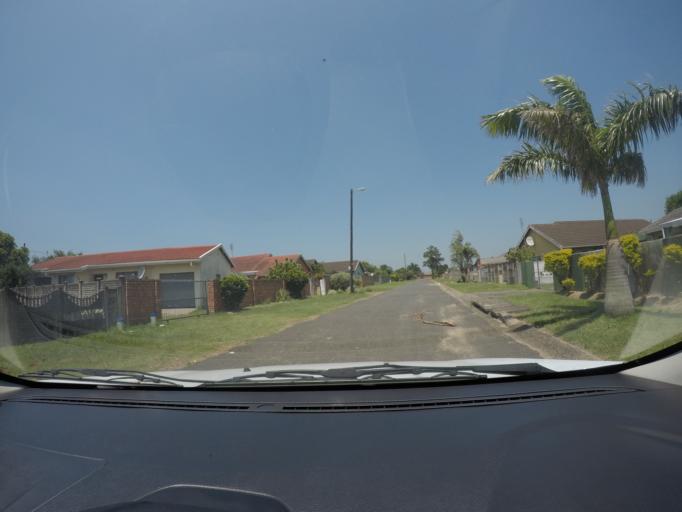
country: ZA
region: KwaZulu-Natal
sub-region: uThungulu District Municipality
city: eSikhawini
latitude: -28.8727
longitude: 31.9161
